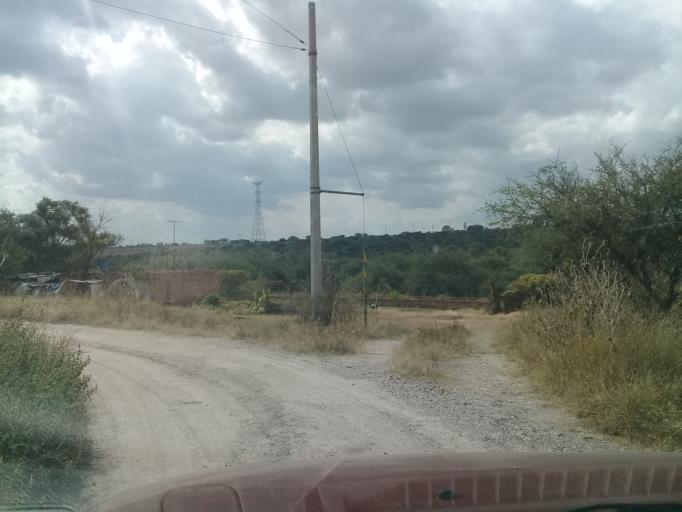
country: MX
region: Aguascalientes
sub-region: Aguascalientes
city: San Sebastian [Fraccionamiento]
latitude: 21.7941
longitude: -102.3356
